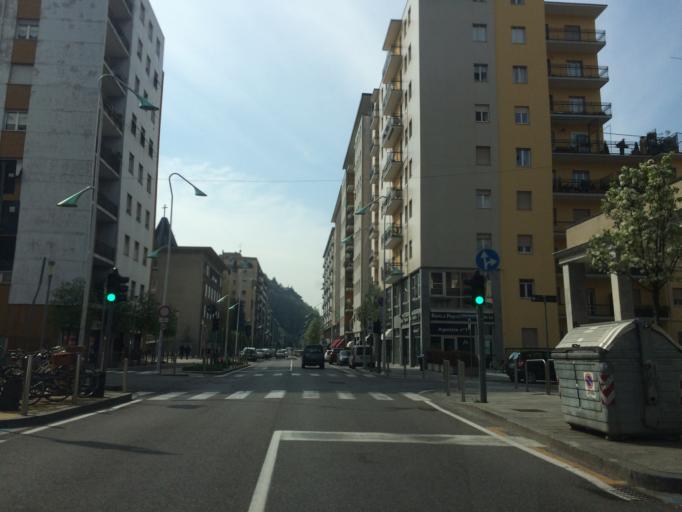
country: IT
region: Lombardy
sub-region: Provincia di Brescia
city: Brescia
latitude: 45.5487
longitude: 10.2264
